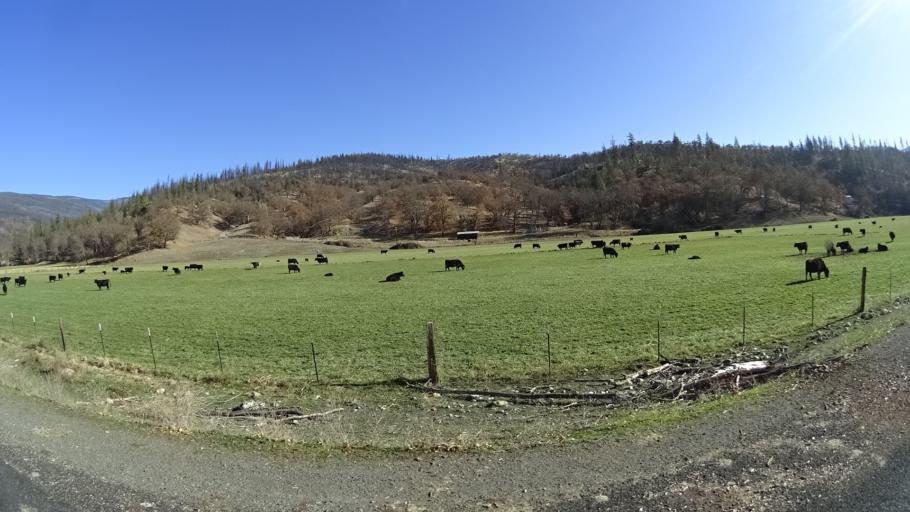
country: US
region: California
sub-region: Siskiyou County
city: Happy Camp
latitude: 41.8311
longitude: -123.0070
